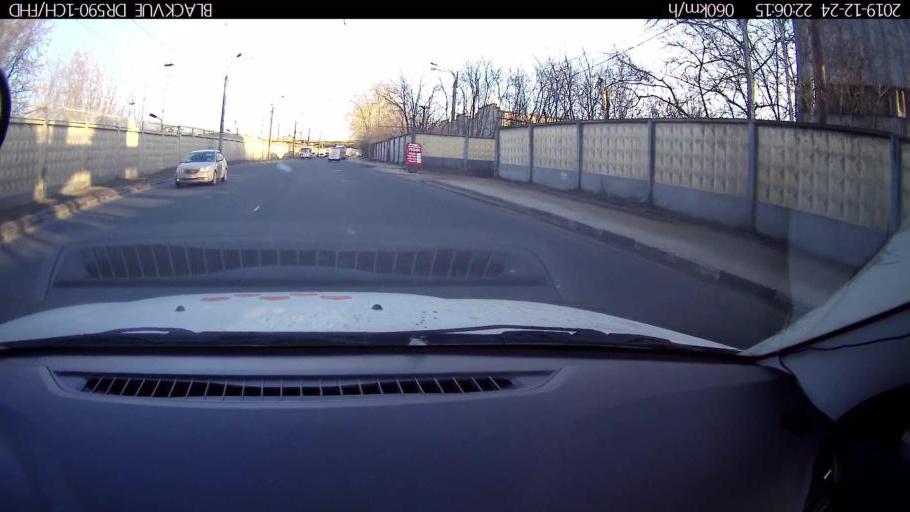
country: RU
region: Nizjnij Novgorod
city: Nizhniy Novgorod
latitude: 56.2418
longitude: 43.8972
